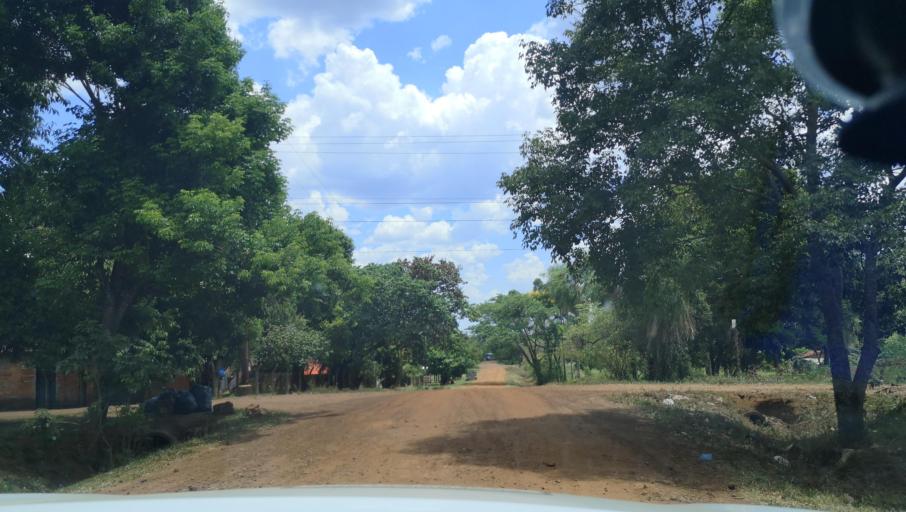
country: PY
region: Itapua
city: Carmen del Parana
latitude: -27.1697
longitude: -56.2380
